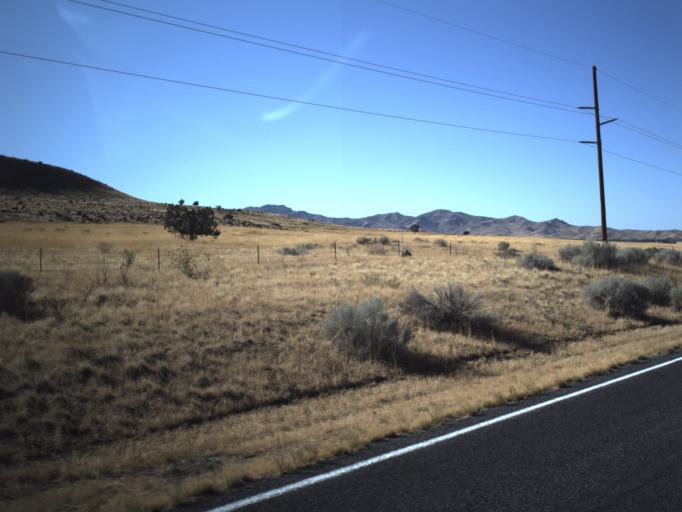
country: US
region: Utah
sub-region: Millard County
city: Delta
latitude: 39.4391
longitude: -112.3171
